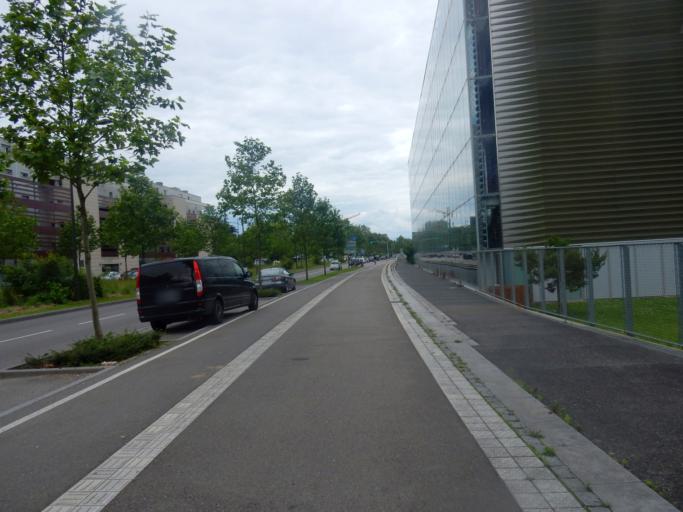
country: FR
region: Alsace
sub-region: Departement du Bas-Rhin
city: Strasbourg
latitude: 48.5714
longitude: 7.7726
